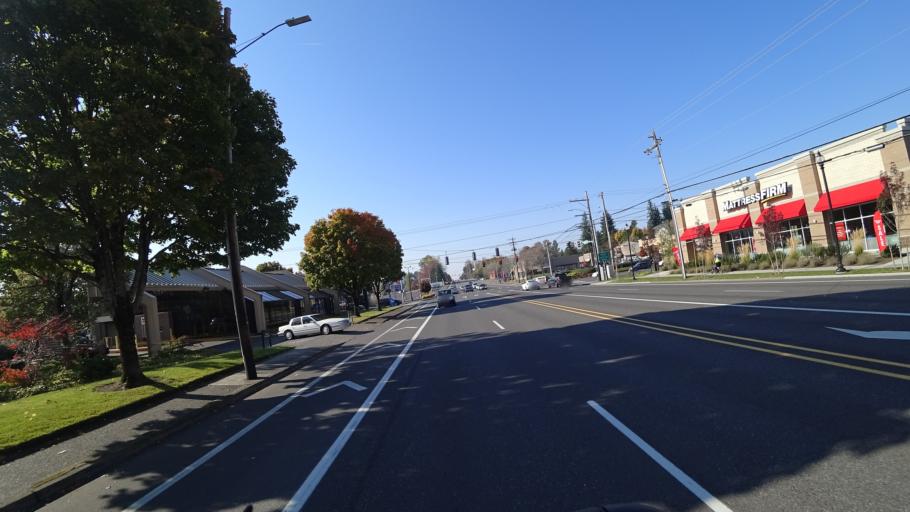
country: US
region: Oregon
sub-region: Multnomah County
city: Gresham
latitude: 45.5096
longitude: -122.4340
